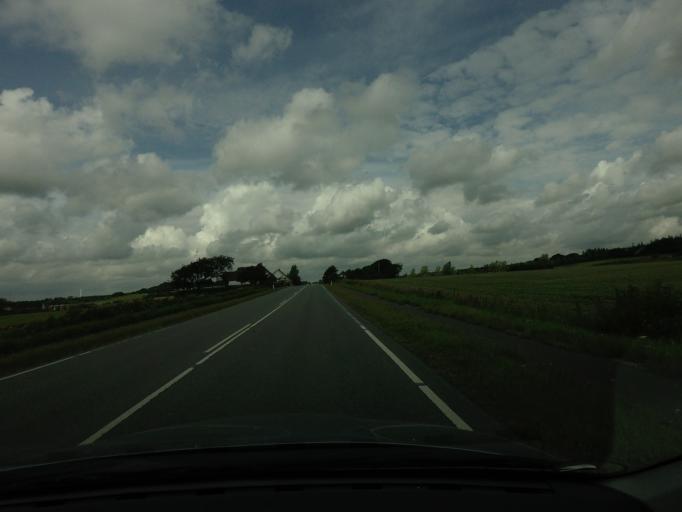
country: DK
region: North Denmark
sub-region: Hjorring Kommune
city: Tars
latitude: 57.3730
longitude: 10.1673
